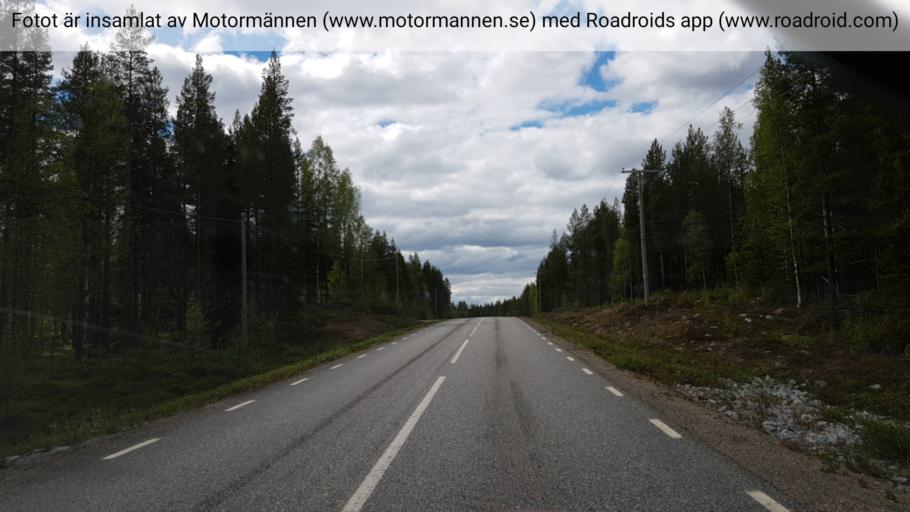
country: SE
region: Vaesterbotten
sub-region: Skelleftea Kommun
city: Langsele
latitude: 64.7638
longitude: 19.9826
